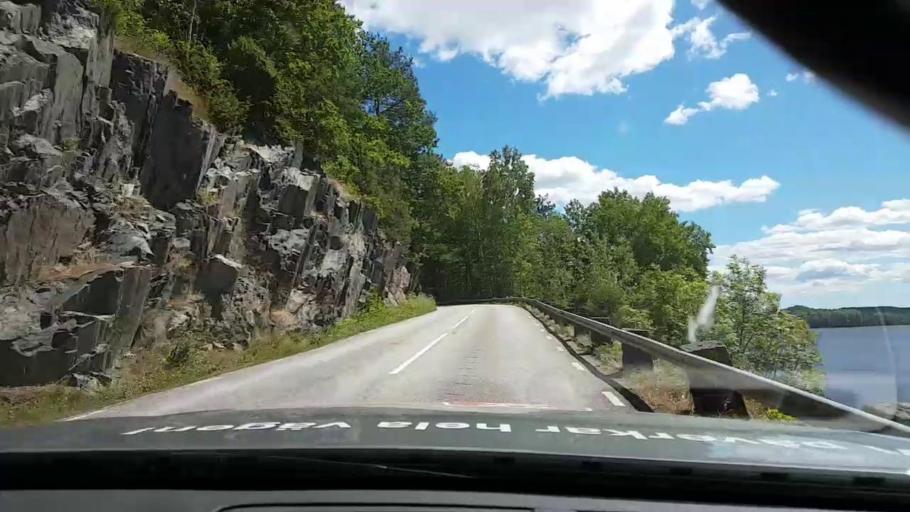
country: SE
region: Kalmar
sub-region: Vasterviks Kommun
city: Overum
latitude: 58.0720
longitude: 16.3739
